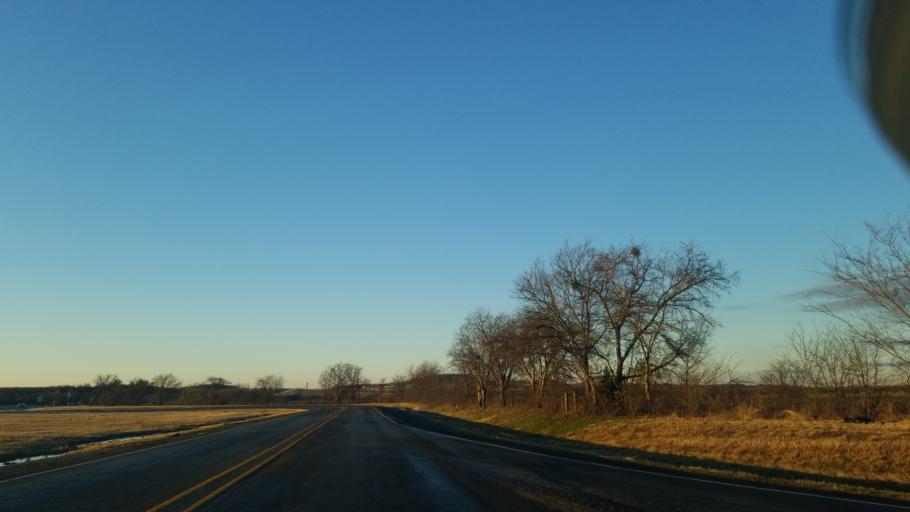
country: US
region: Texas
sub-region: Denton County
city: Argyle
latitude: 33.1718
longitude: -97.1829
